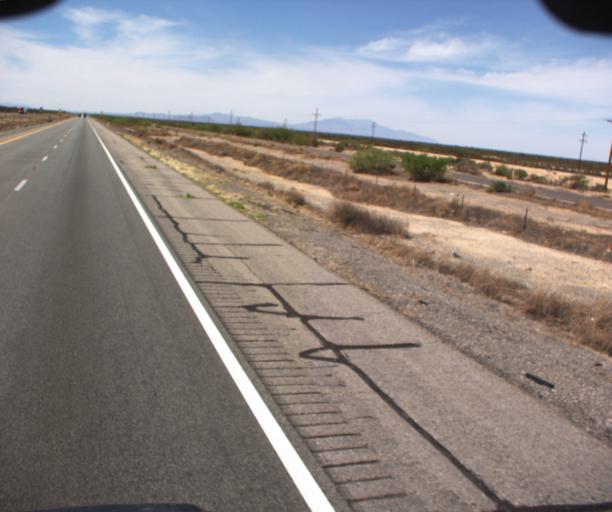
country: US
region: Arizona
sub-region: Cochise County
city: Willcox
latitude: 32.2876
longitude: -109.3107
